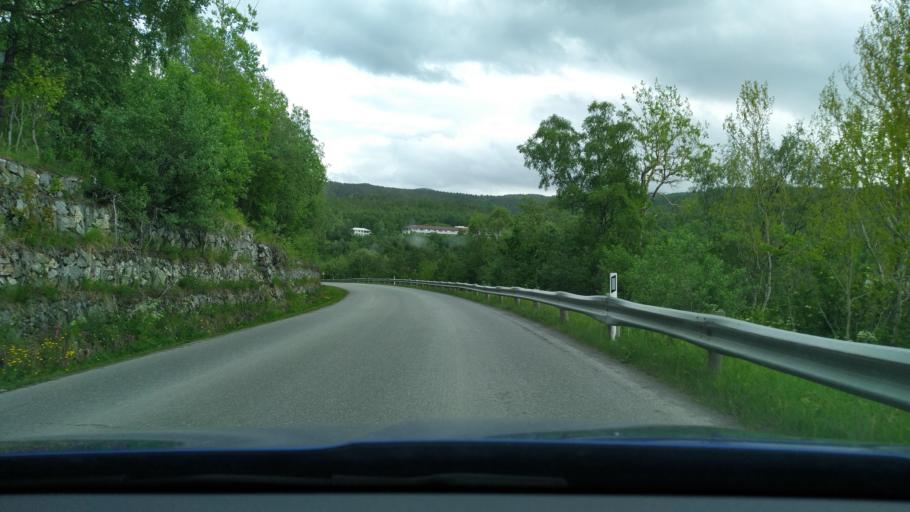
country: NO
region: Troms
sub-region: Salangen
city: Sjovegan
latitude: 68.8672
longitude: 17.8538
